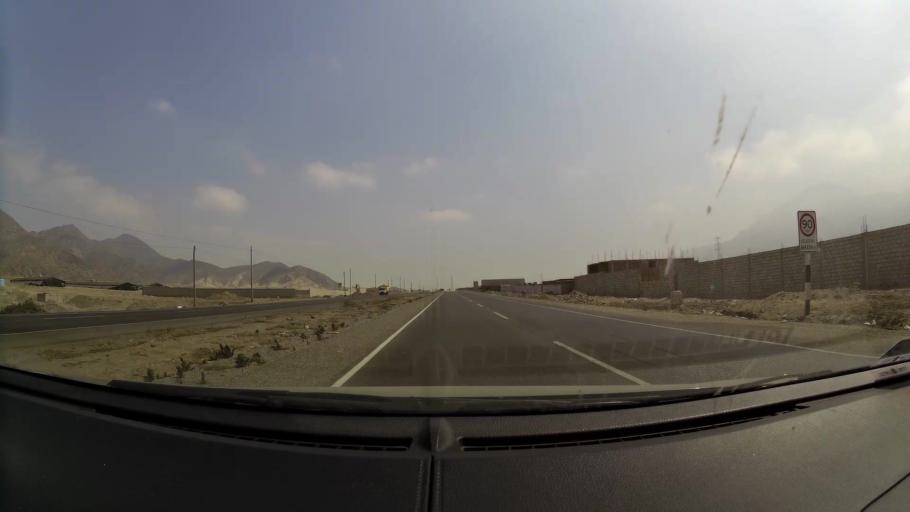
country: PE
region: La Libertad
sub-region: Ascope
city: Chicama
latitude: -7.9509
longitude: -79.0919
